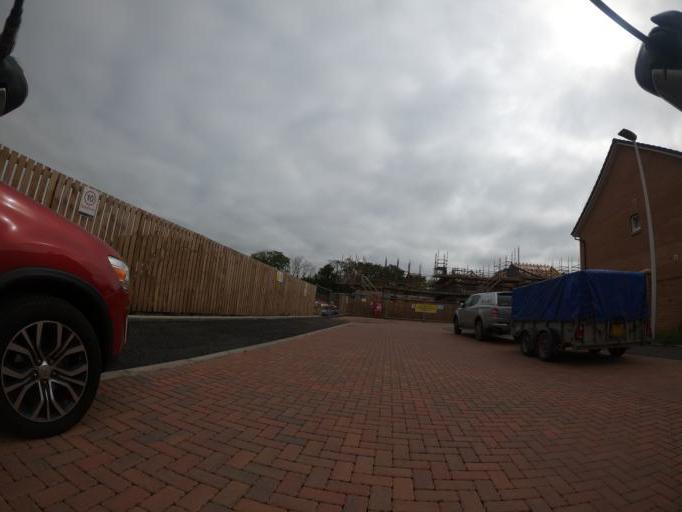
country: GB
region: Scotland
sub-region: East Lothian
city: Musselburgh
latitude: 55.9336
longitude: -3.0859
